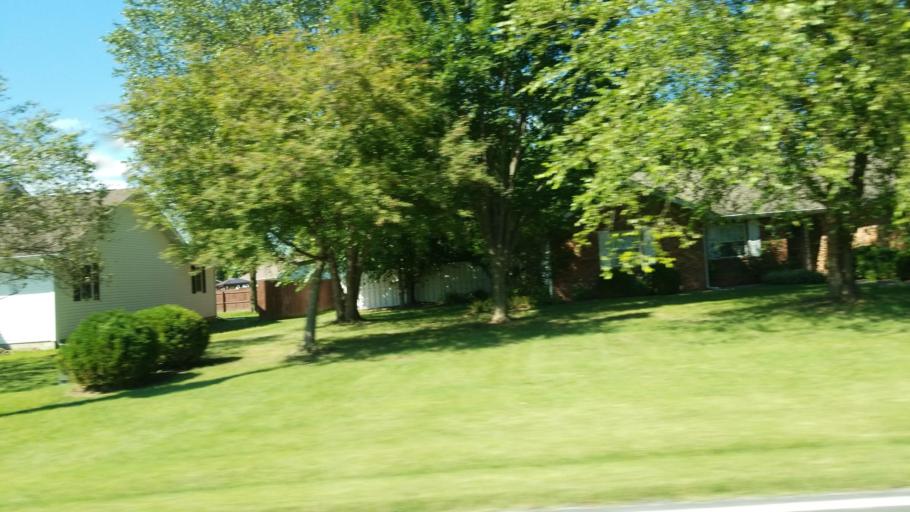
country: US
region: Illinois
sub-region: Williamson County
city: Marion
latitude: 37.7427
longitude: -88.9007
